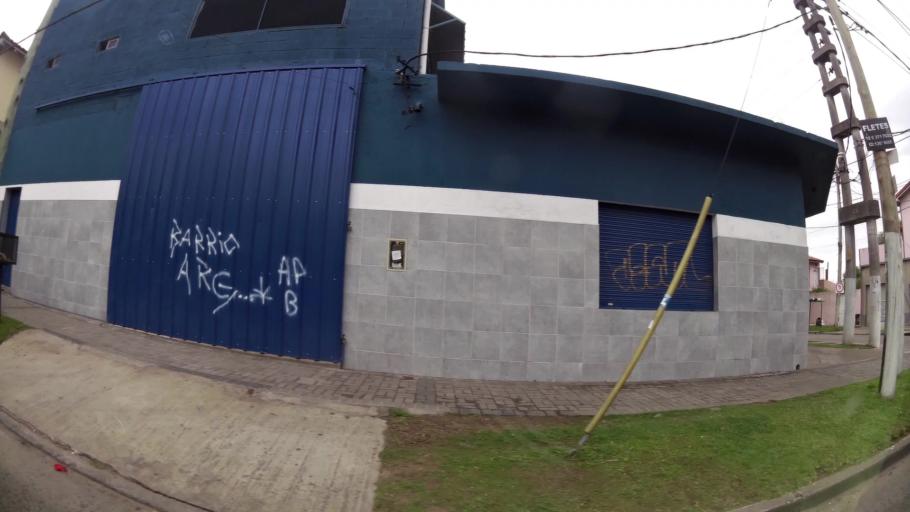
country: AR
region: Buenos Aires
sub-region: Partido de Quilmes
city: Quilmes
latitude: -34.7797
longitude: -58.2430
